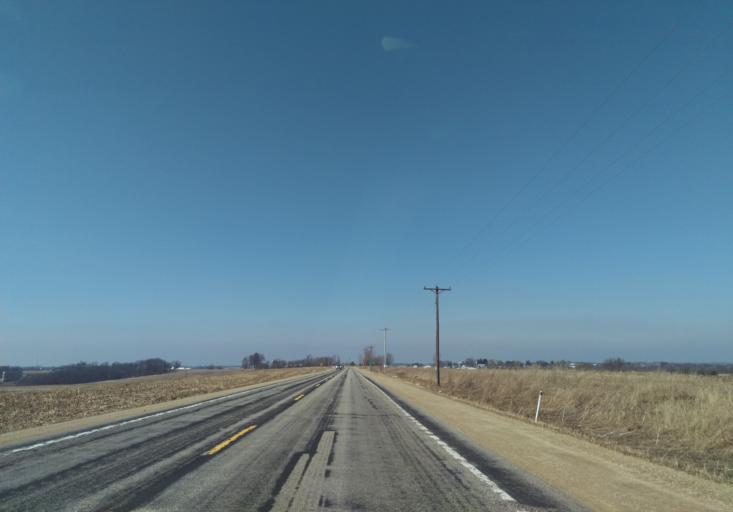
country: US
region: Wisconsin
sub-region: Vernon County
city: Westby
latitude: 43.6640
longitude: -90.8659
